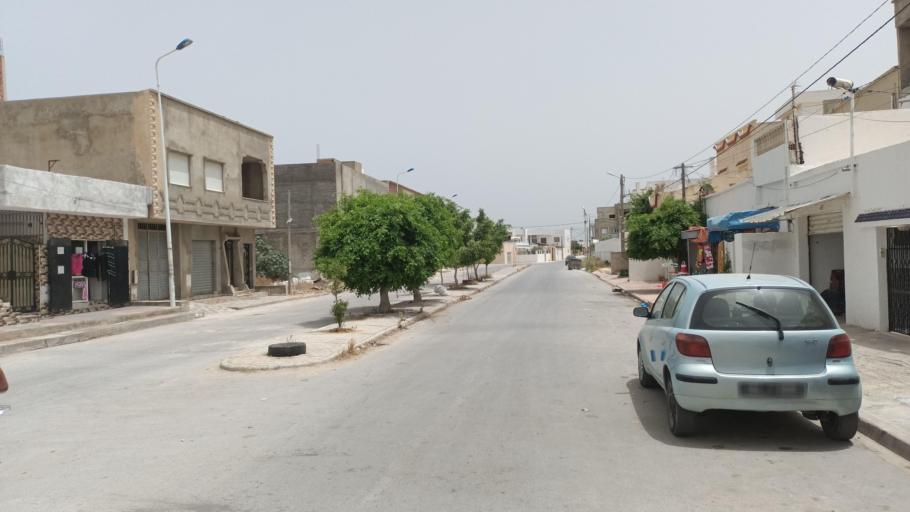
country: TN
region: Nabul
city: Manzil Bu Zalafah
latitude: 36.7022
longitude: 10.4917
